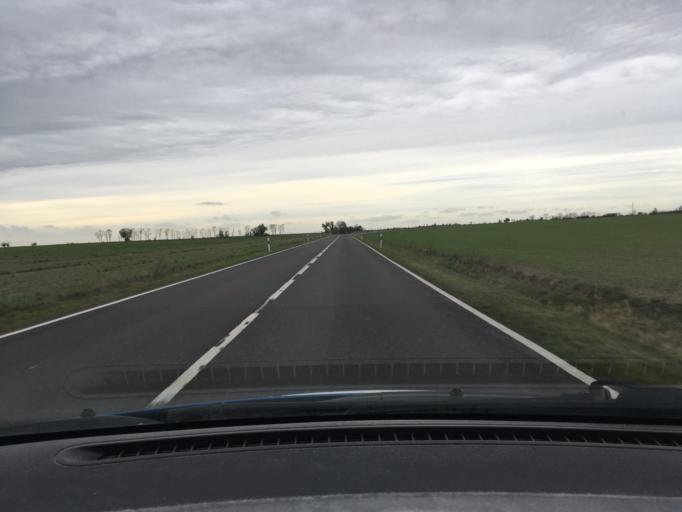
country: DE
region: Saxony-Anhalt
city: Leitzkau
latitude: 52.0384
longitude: 11.9808
